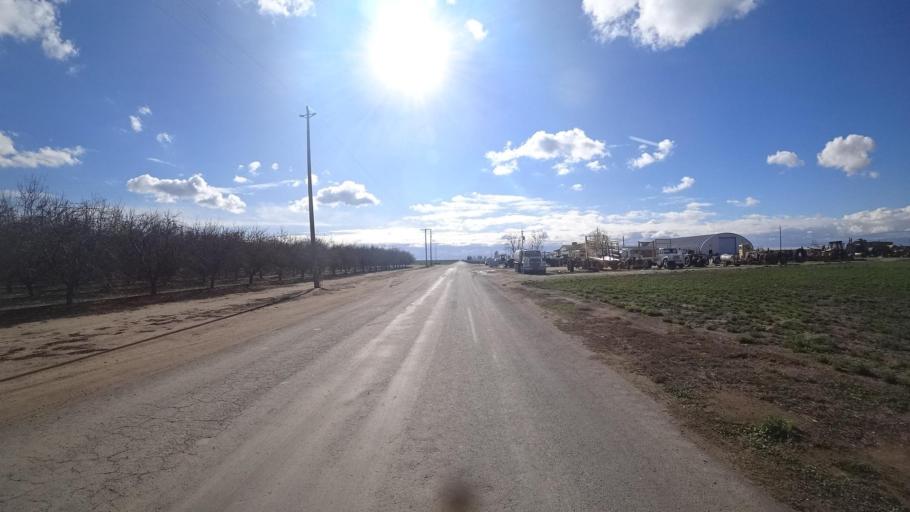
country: US
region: California
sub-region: Kern County
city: Greenfield
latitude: 35.2538
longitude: -119.1284
